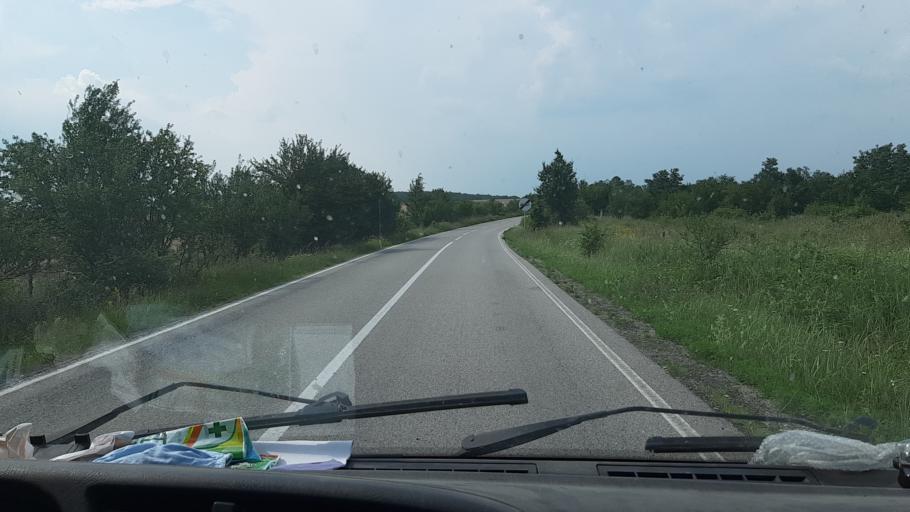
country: RO
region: Timis
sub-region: Comuna Victor Vlad Delamarina
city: Victor Vlad Delamarina
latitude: 45.5663
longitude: 21.8720
